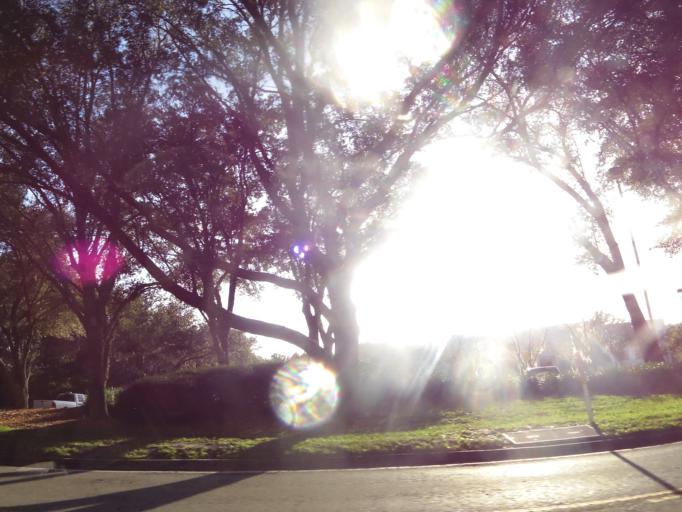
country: US
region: Florida
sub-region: Duval County
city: Jacksonville
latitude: 30.2588
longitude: -81.6009
